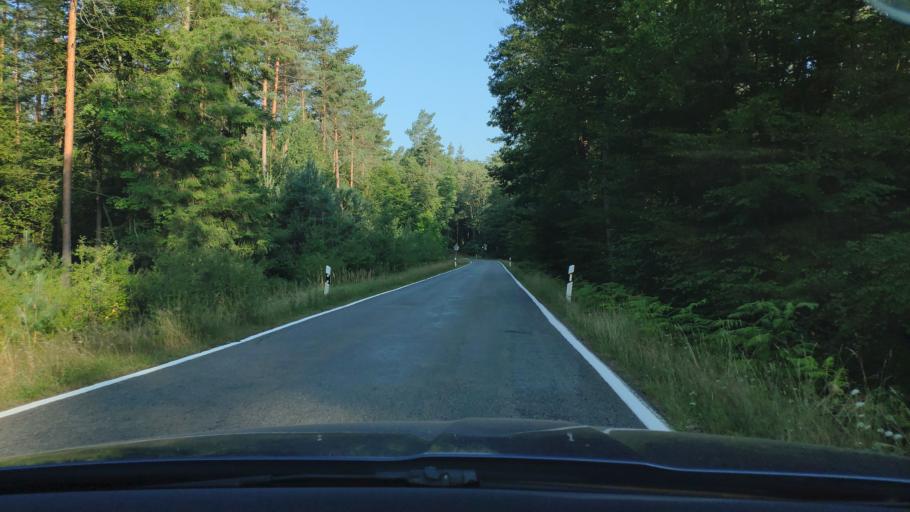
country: DE
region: Rheinland-Pfalz
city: Eppenbrunn
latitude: 49.1126
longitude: 7.5821
